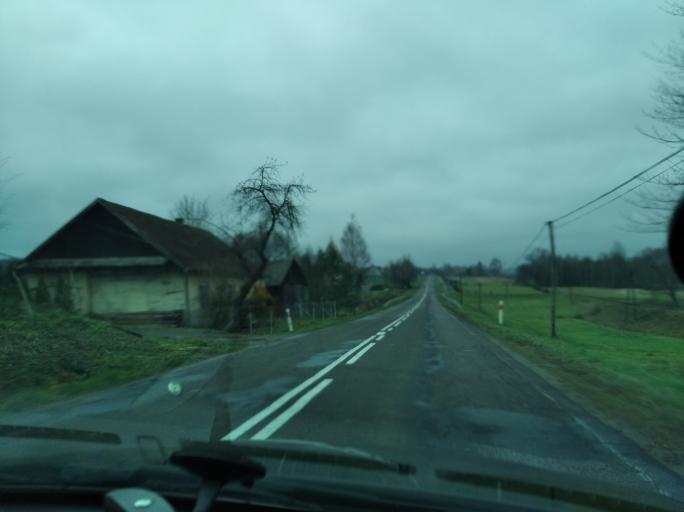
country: PL
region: Subcarpathian Voivodeship
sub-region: Powiat rzeszowski
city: Dynow
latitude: 49.8579
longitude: 22.2497
